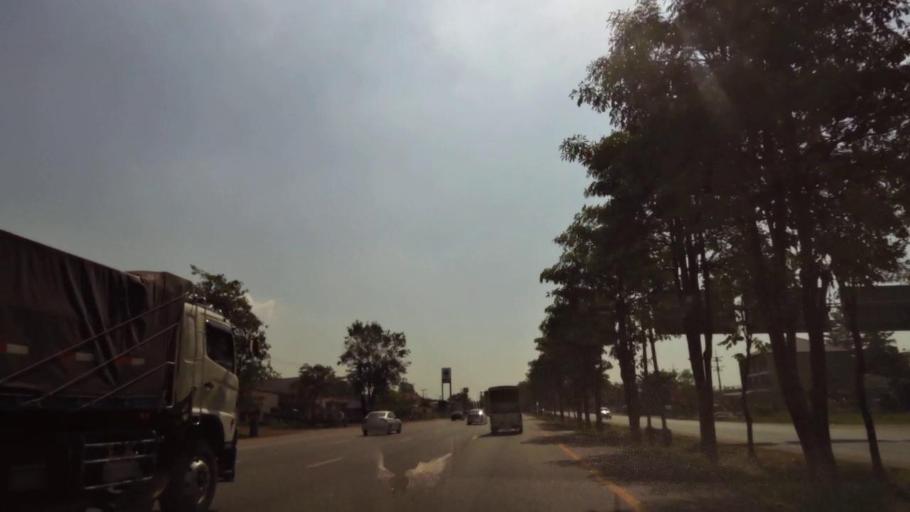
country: TH
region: Phichit
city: Bueng Na Rang
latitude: 16.1210
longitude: 100.1257
